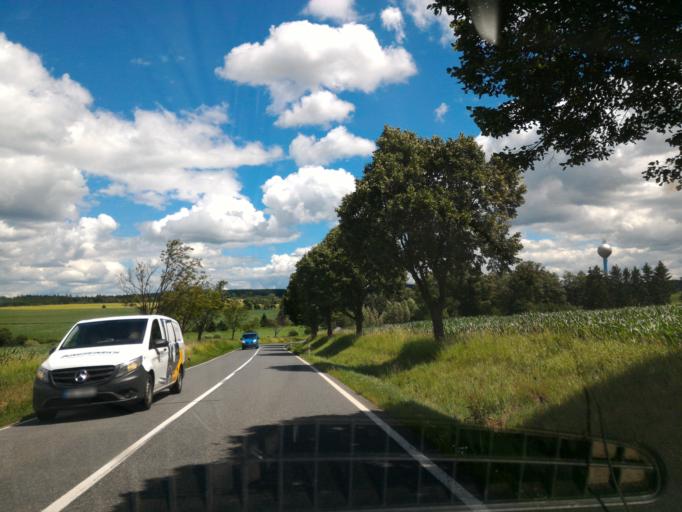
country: CZ
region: Vysocina
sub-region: Okres Jihlava
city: Polna
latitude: 49.4424
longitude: 15.7564
